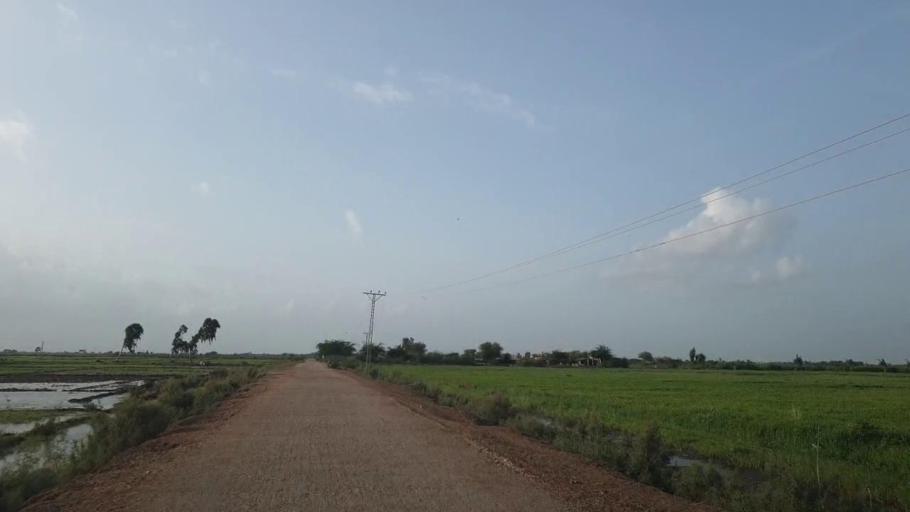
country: PK
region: Sindh
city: Tando Bago
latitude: 24.6580
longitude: 69.1119
